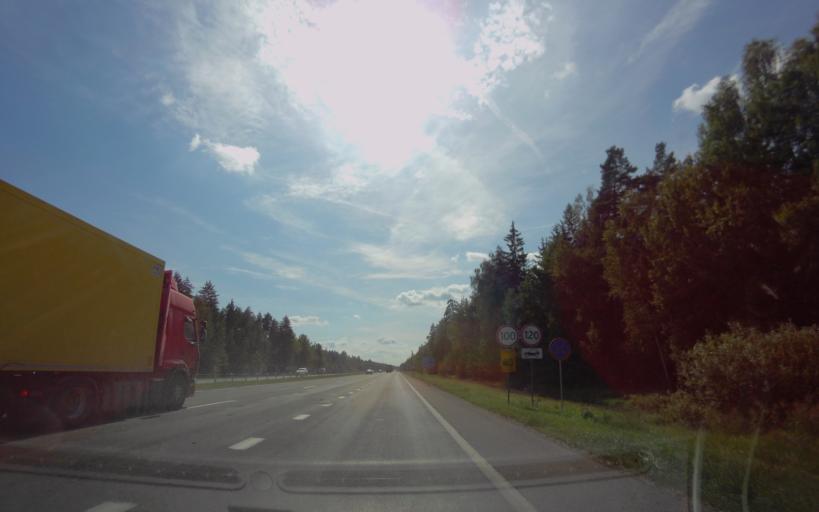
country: BY
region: Minsk
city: Horad Barysaw
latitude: 54.1728
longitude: 28.5724
